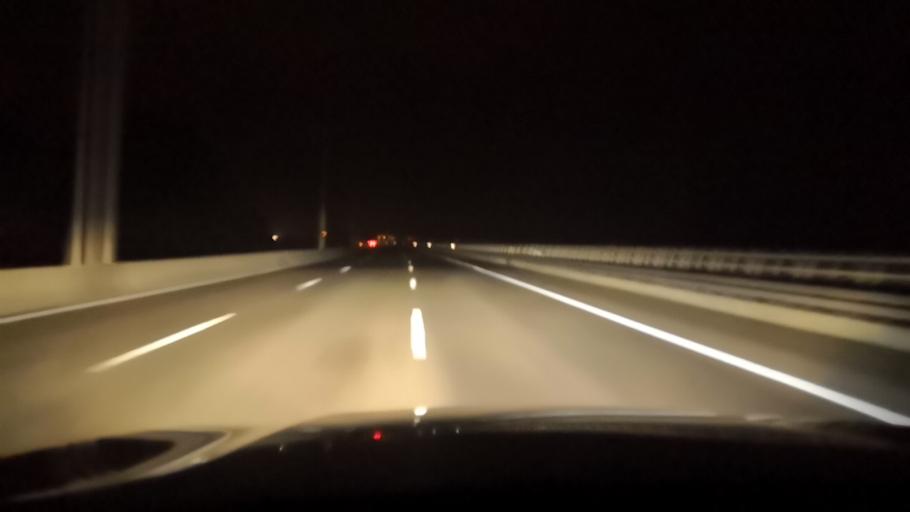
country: PT
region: Santarem
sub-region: Benavente
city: Samora Correia
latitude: 38.9682
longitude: -8.8664
